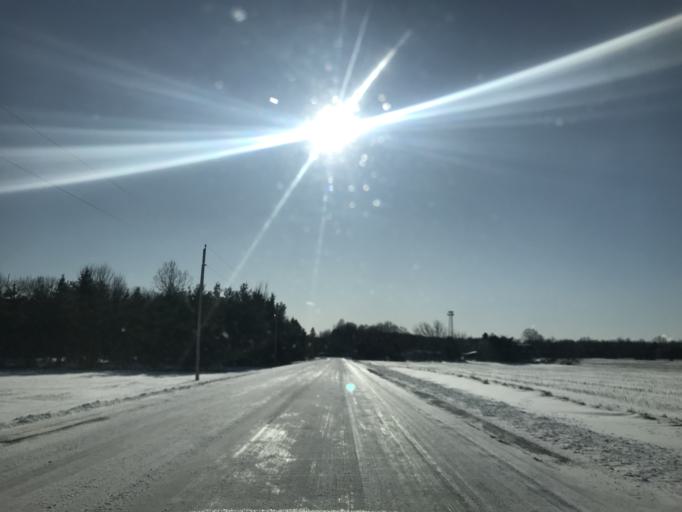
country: US
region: Wisconsin
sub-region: Door County
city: Sturgeon Bay
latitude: 44.8264
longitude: -87.5041
